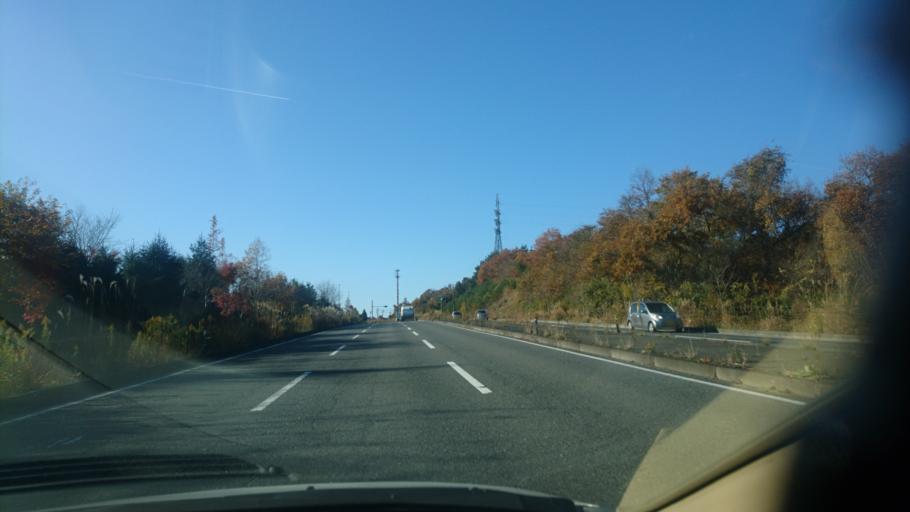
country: JP
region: Miyagi
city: Tomiya
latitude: 38.4733
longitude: 140.9025
